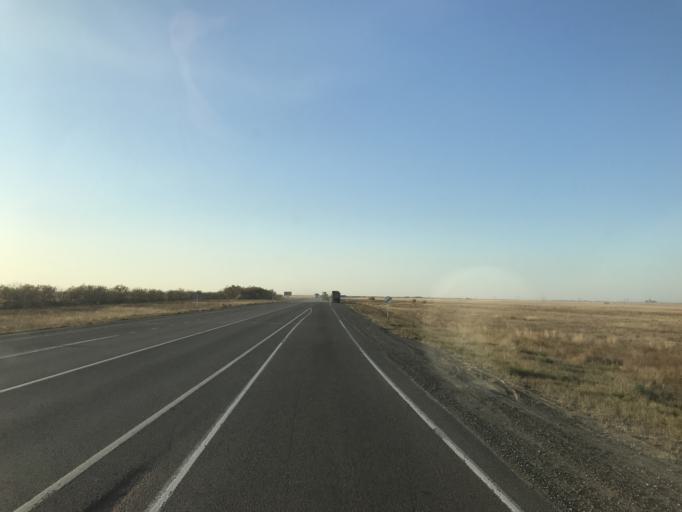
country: KZ
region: Pavlodar
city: Leninskiy
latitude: 52.1558
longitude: 76.8178
